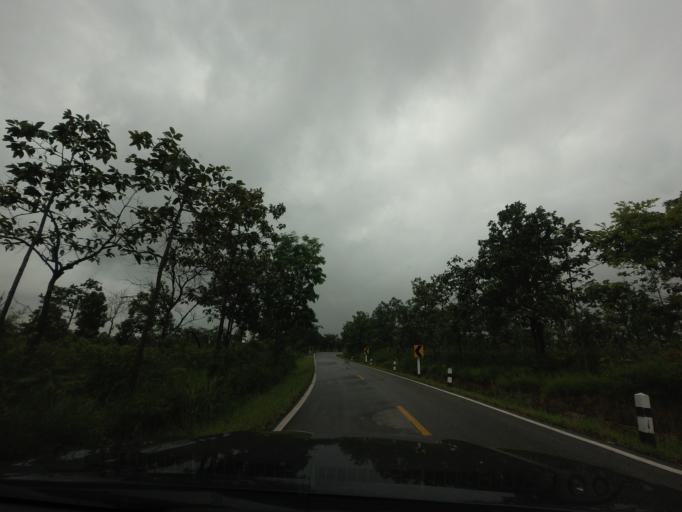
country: TH
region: Nong Khai
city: Sangkhom
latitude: 18.0354
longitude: 102.3372
